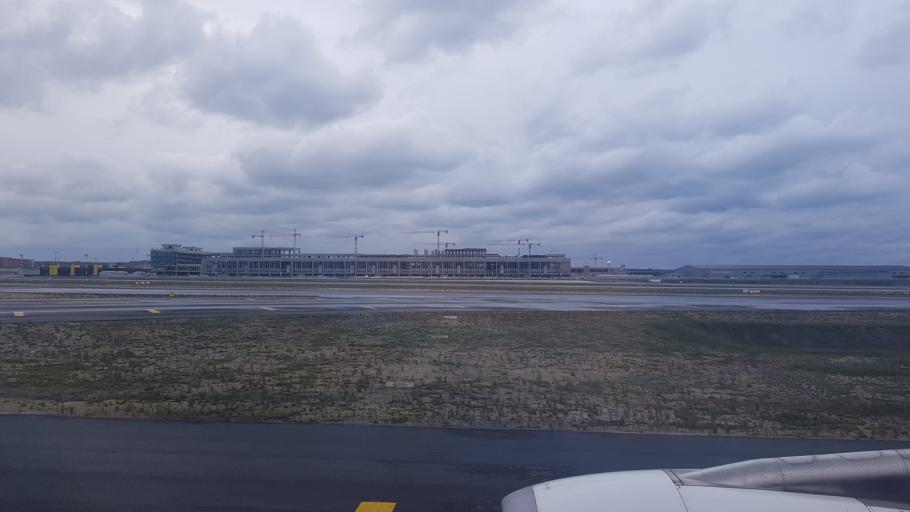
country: TR
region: Istanbul
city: Durusu
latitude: 41.2781
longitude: 28.7296
